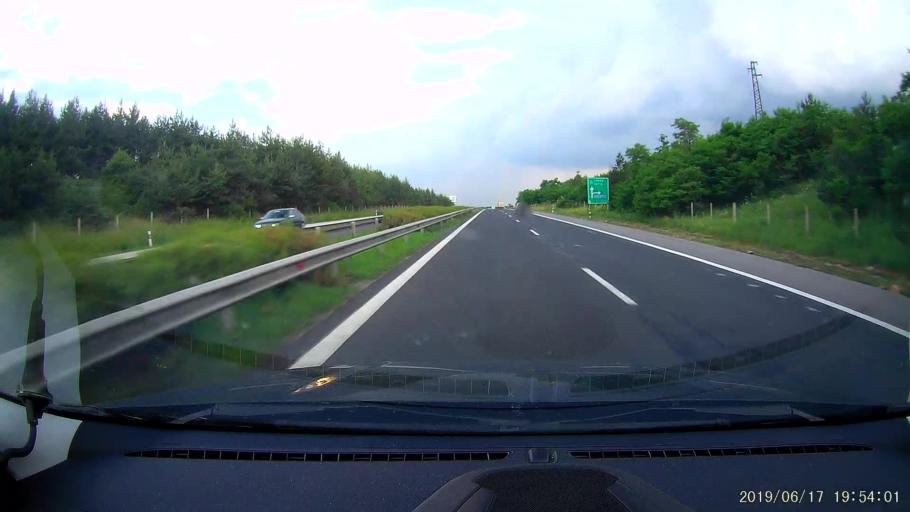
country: BG
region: Sofiya
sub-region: Obshtina Gorna Malina
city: Gorna Malina
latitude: 42.5484
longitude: 23.7067
